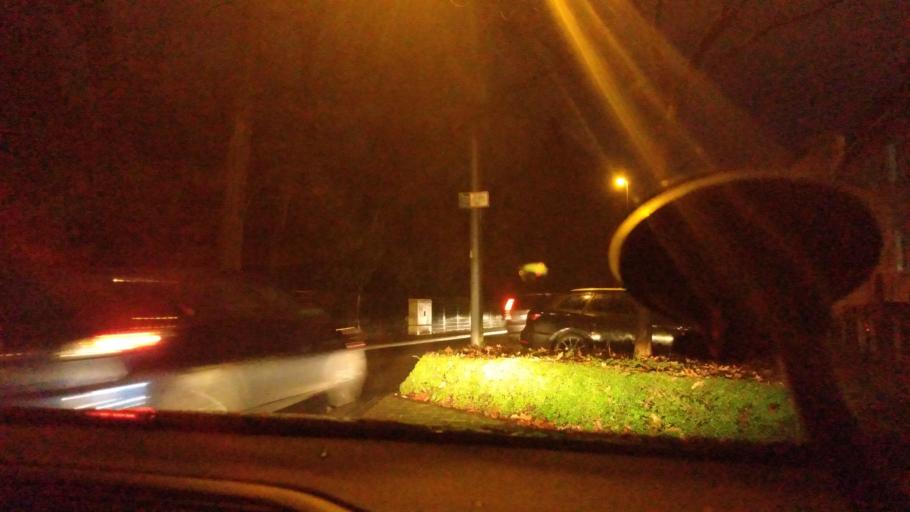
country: DE
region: North Rhine-Westphalia
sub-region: Regierungsbezirk Koln
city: Neustadt/Sued
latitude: 50.9014
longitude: 6.9409
